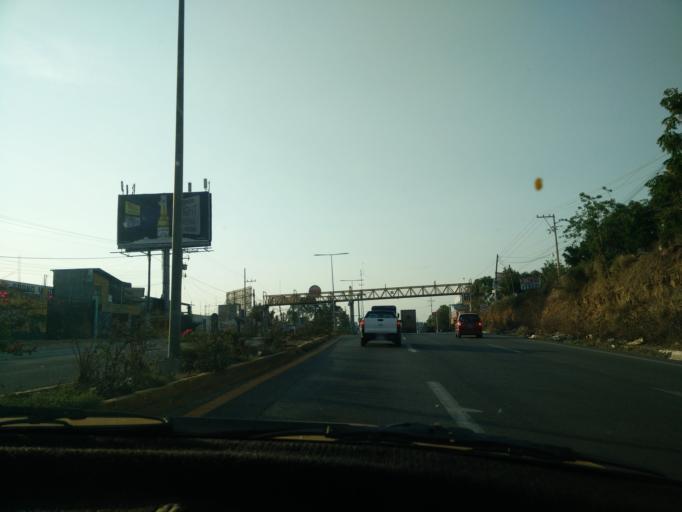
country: MX
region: Oaxaca
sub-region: Santa Maria Atzompa
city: Fraccionamiento Riberas de San Jeronimo
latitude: 17.1353
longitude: -96.7745
